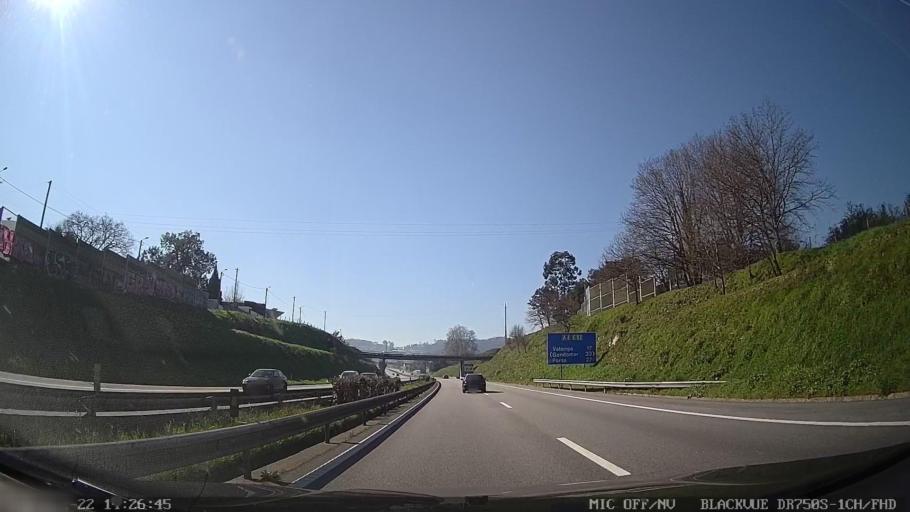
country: PT
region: Porto
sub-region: Paredes
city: Casteloes de Cepeda
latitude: 41.1993
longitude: -8.3442
